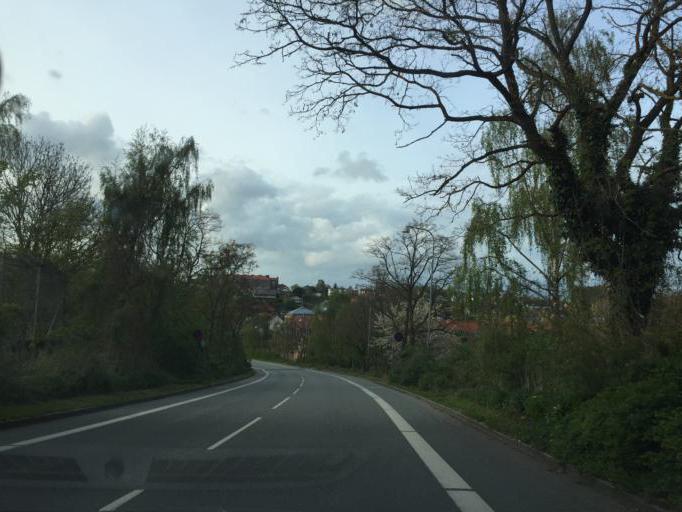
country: DK
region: South Denmark
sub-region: Svendborg Kommune
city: Svendborg
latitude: 55.0619
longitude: 10.6086
